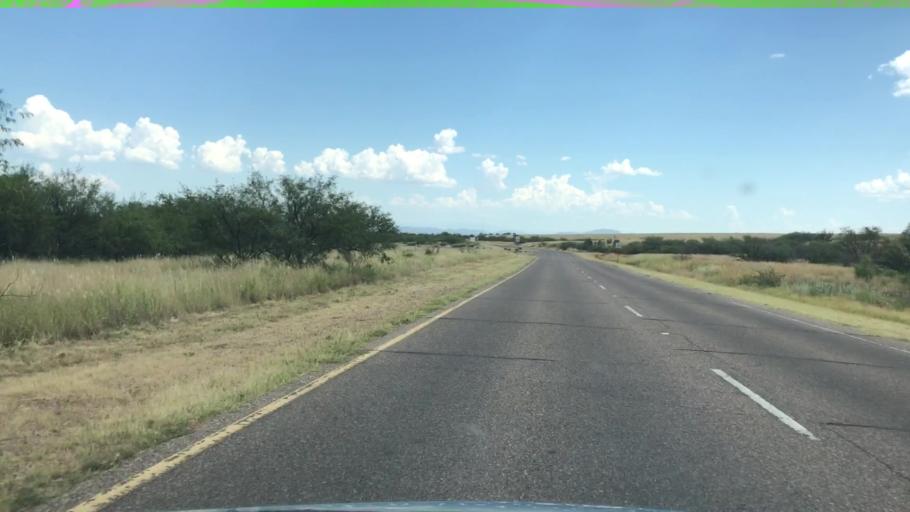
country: US
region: Arizona
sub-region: Cochise County
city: Sierra Vista
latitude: 31.5438
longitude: -110.3298
